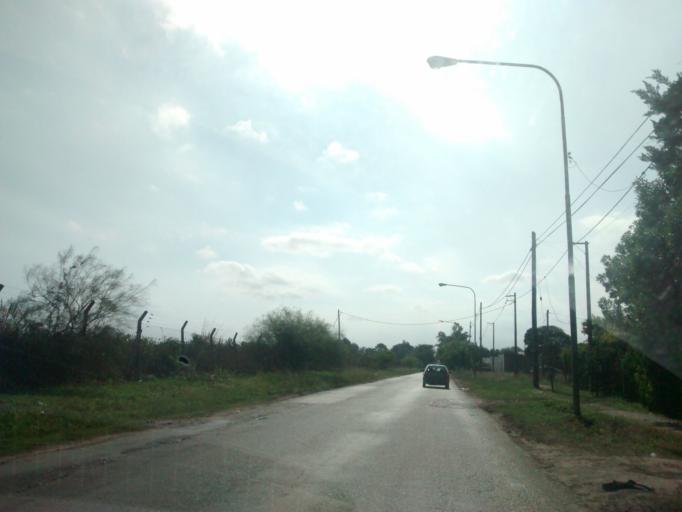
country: AR
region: Buenos Aires
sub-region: Partido de La Plata
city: La Plata
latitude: -34.9614
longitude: -57.8880
